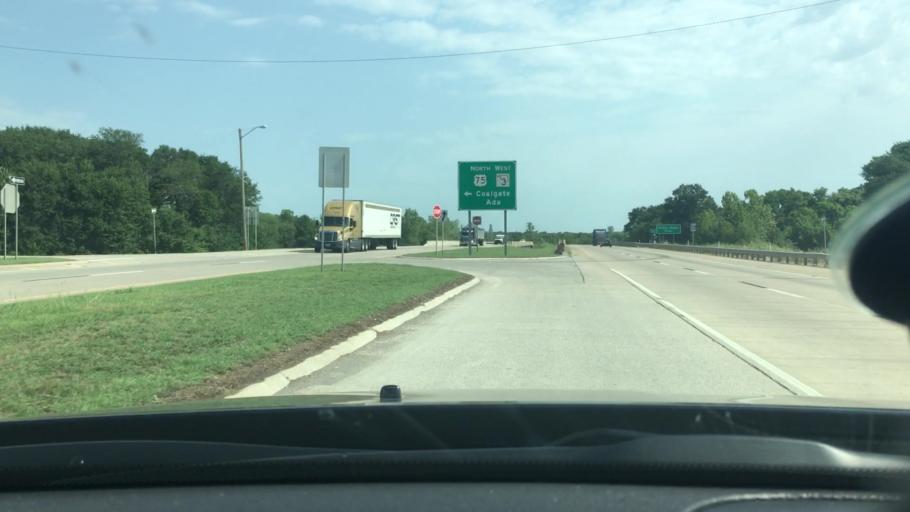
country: US
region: Oklahoma
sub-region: Atoka County
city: Atoka
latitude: 34.3925
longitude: -96.1256
